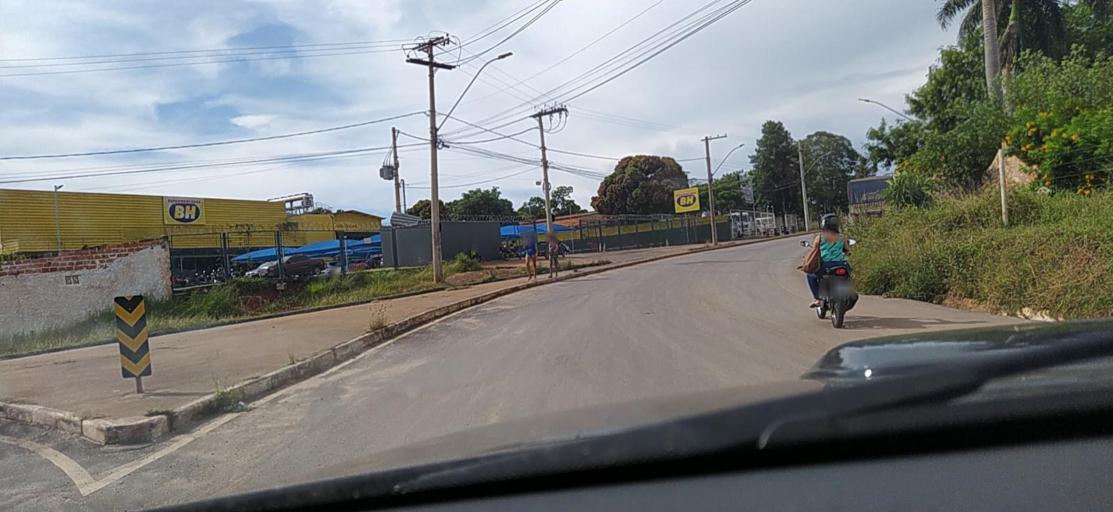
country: BR
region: Minas Gerais
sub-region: Montes Claros
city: Montes Claros
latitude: -16.7456
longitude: -43.8462
